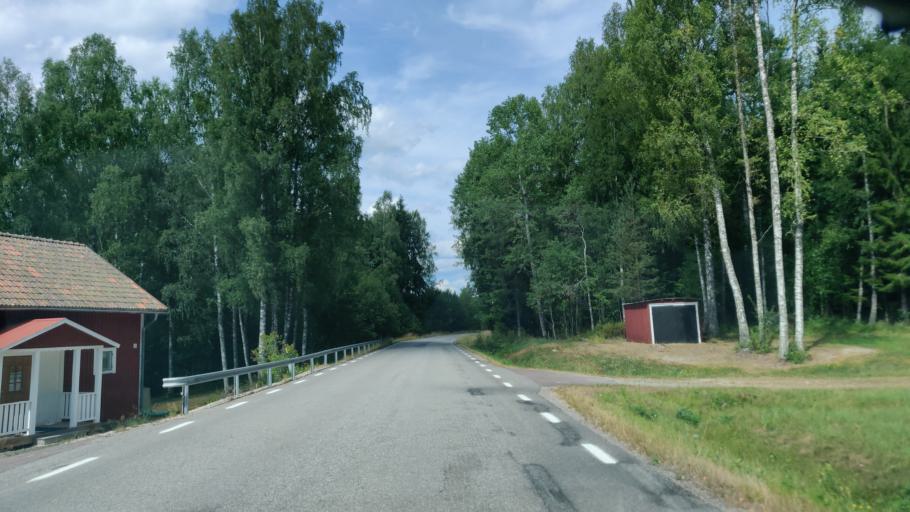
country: SE
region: Vaermland
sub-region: Hagfors Kommun
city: Ekshaerad
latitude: 60.1000
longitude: 13.5020
